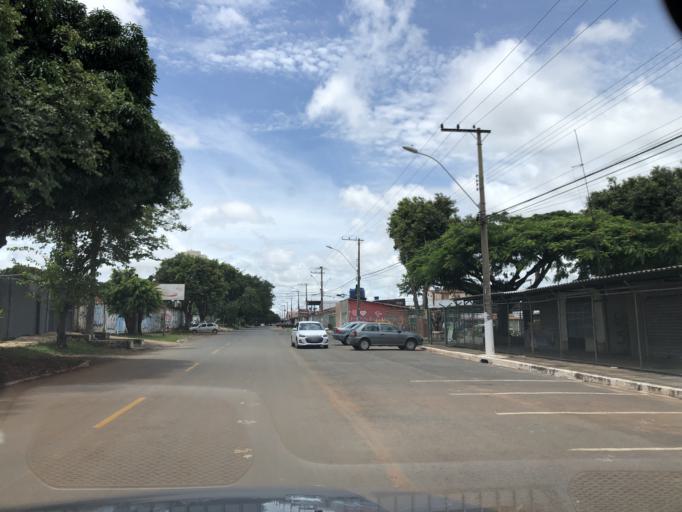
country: BR
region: Federal District
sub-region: Brasilia
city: Brasilia
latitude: -15.8392
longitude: -48.1099
